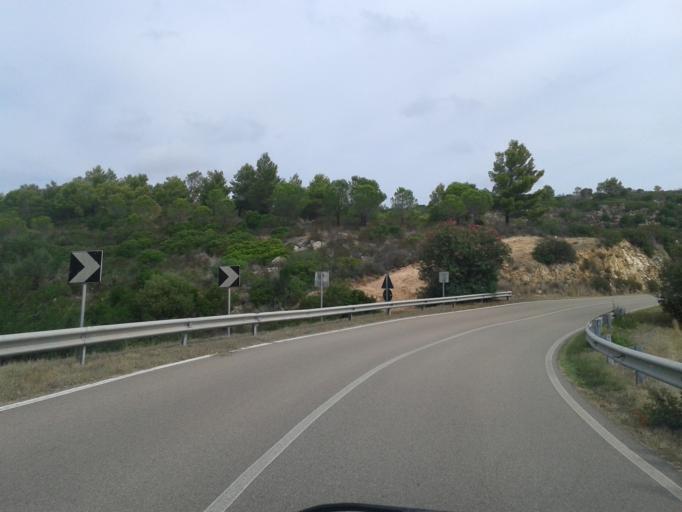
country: IT
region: Sardinia
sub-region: Provincia di Cagliari
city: Villasimius
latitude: 39.1598
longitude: 9.5610
